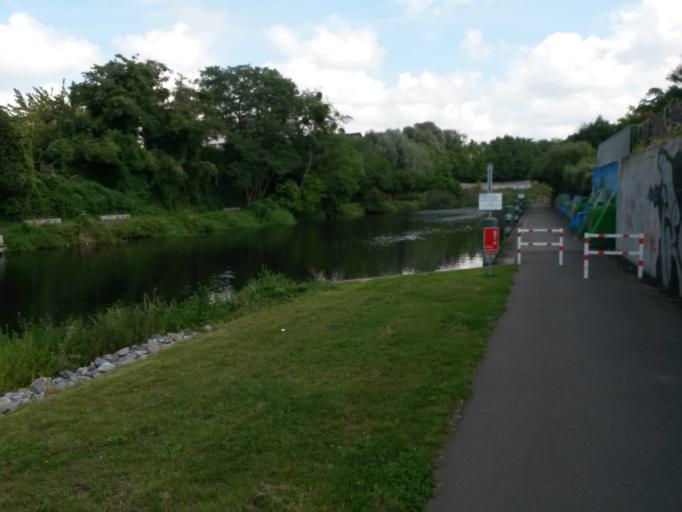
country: DE
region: Brandenburg
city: Eberswalde
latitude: 52.8366
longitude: 13.8110
